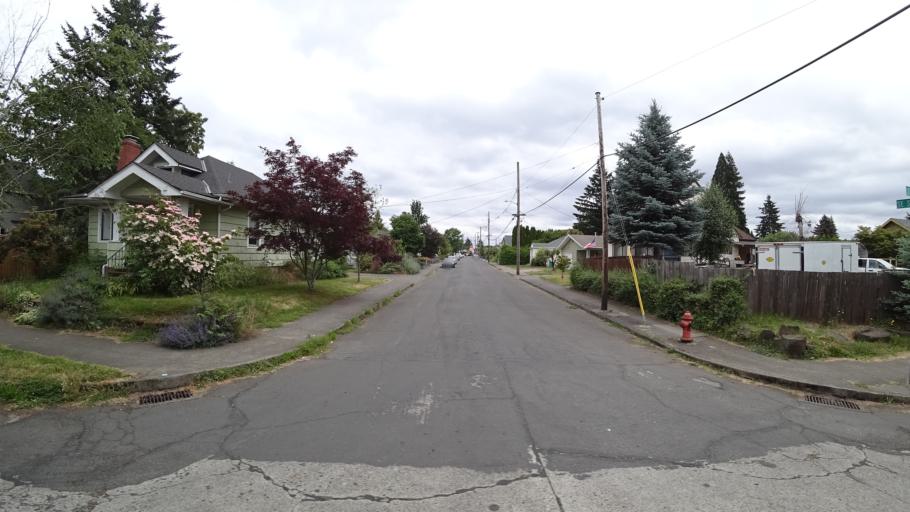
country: US
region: Oregon
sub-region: Multnomah County
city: Lents
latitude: 45.5141
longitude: -122.5814
